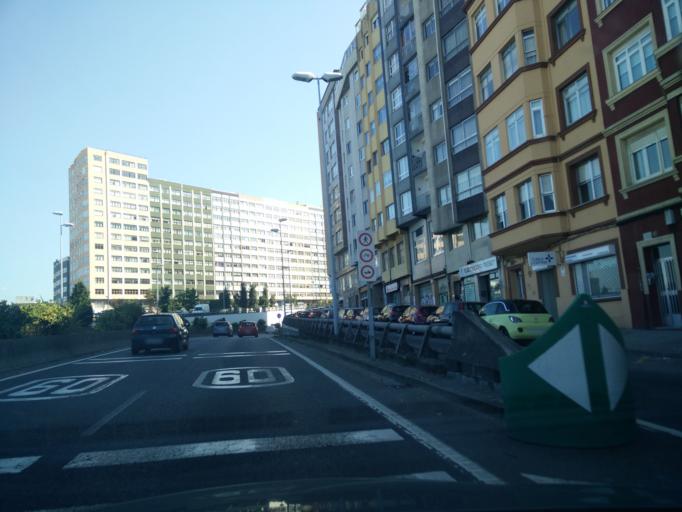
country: ES
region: Galicia
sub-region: Provincia da Coruna
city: A Coruna
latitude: 43.3540
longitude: -8.3929
